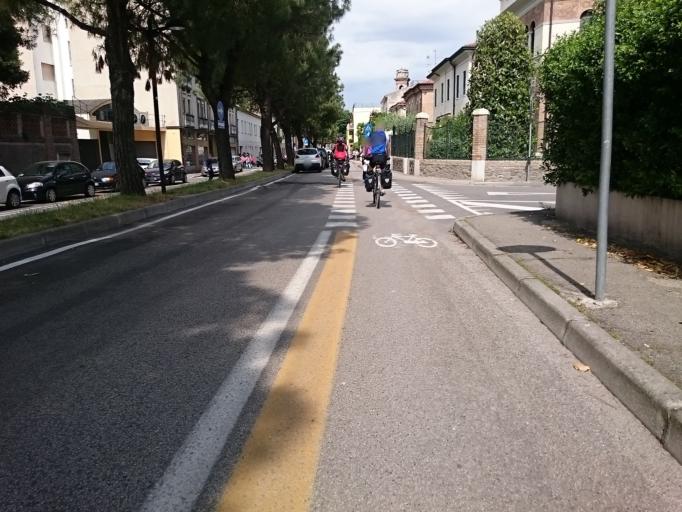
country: IT
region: Veneto
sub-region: Provincia di Padova
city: Este
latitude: 45.2277
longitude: 11.6595
